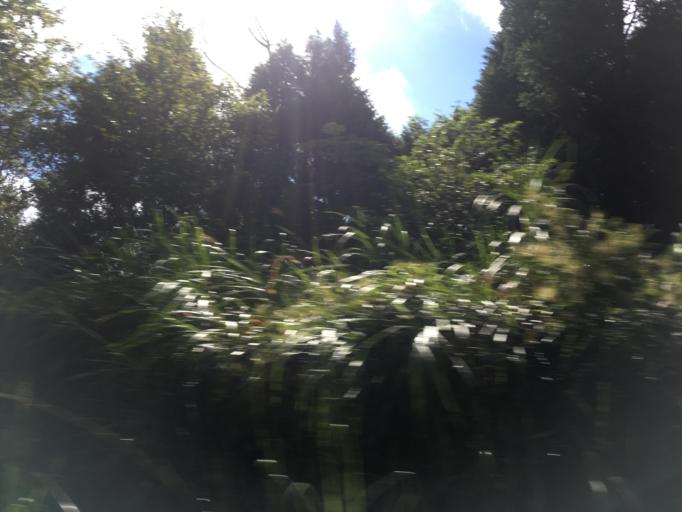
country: TW
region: Taiwan
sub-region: Yilan
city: Yilan
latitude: 24.5118
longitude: 121.5937
